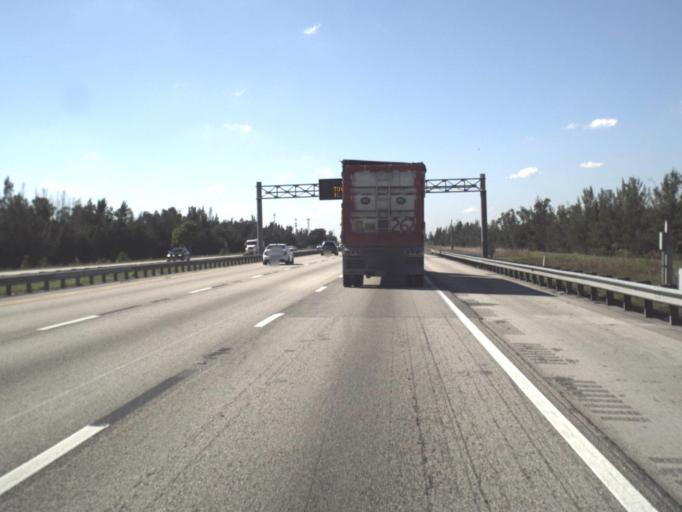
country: US
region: Florida
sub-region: Miami-Dade County
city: Palm Springs North
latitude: 25.9198
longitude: -80.3786
